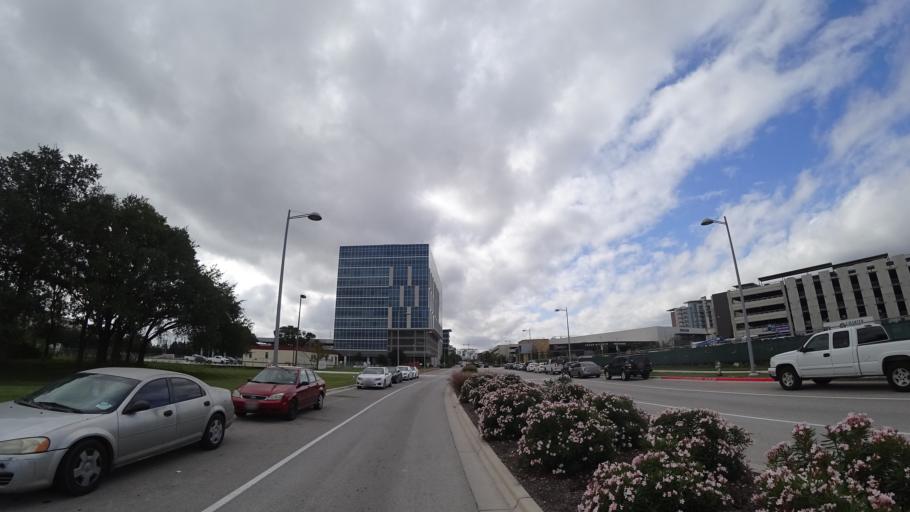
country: US
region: Texas
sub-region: Travis County
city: Wells Branch
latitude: 30.4038
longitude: -97.7187
